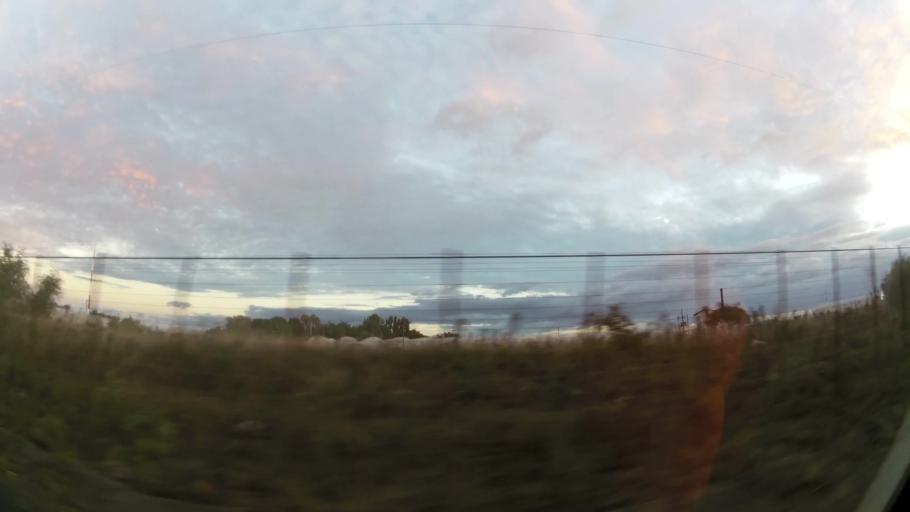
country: ZA
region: Limpopo
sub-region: Capricorn District Municipality
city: Polokwane
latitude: -23.7340
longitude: 29.4185
